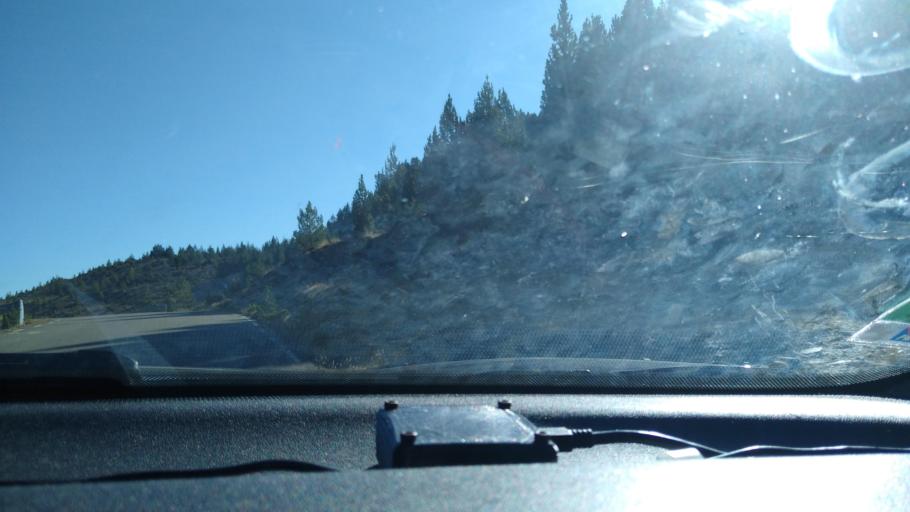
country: ES
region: Catalonia
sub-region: Provincia de Barcelona
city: Saldes
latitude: 42.2006
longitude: 1.7669
